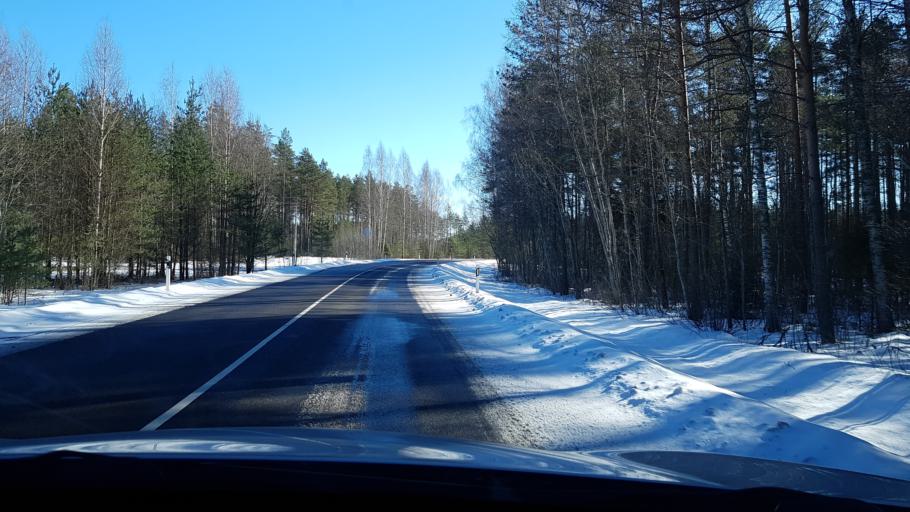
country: EE
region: Polvamaa
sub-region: Raepina vald
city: Rapina
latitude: 57.9932
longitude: 27.5600
